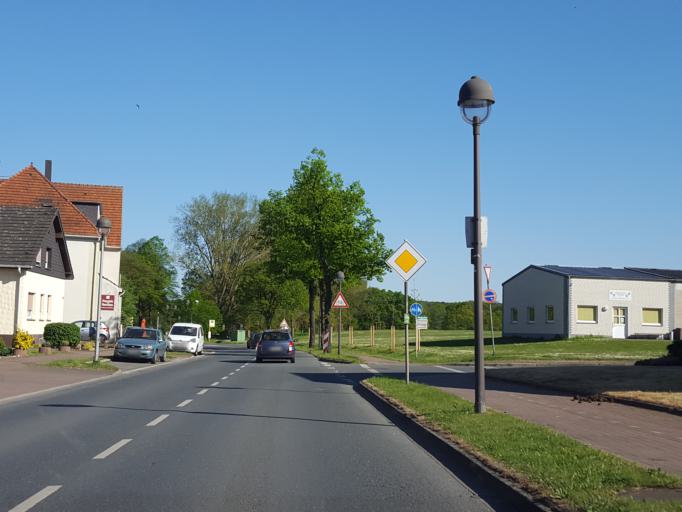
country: DE
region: North Rhine-Westphalia
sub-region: Regierungsbezirk Munster
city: Haltern
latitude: 51.7185
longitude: 7.2341
